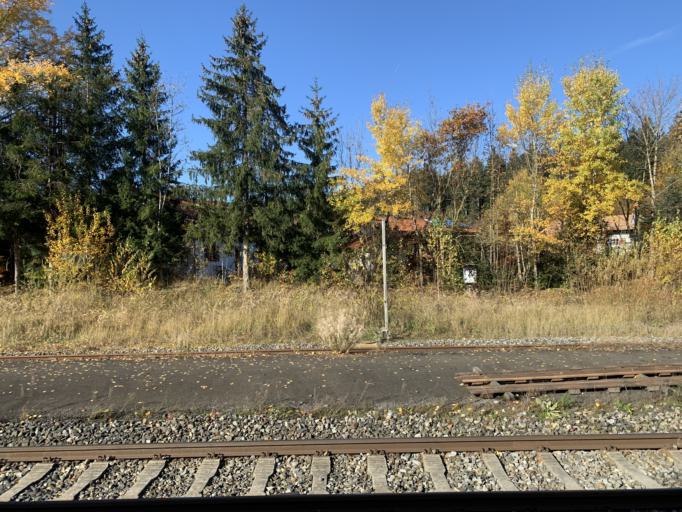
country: DE
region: Bavaria
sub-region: Upper Bavaria
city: Waakirchen
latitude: 47.7965
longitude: 11.6852
